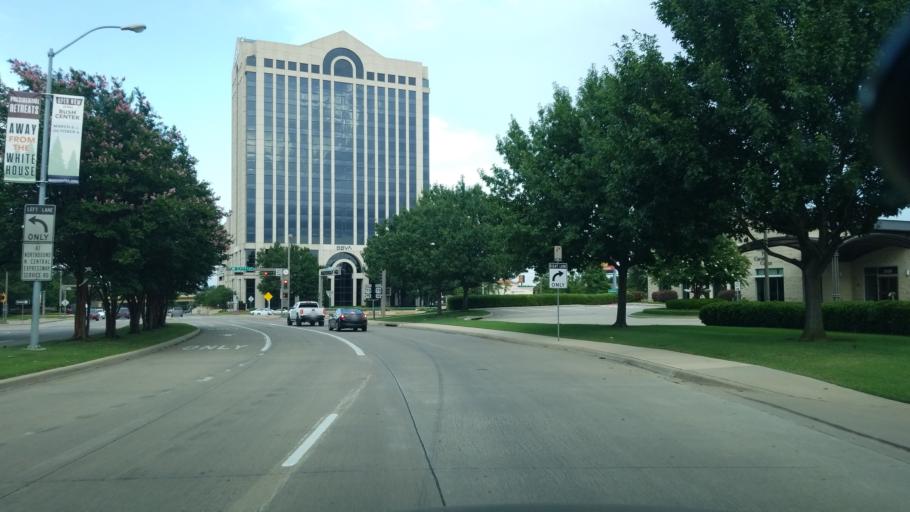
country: US
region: Texas
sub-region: Dallas County
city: University Park
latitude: 32.8609
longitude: -96.7716
